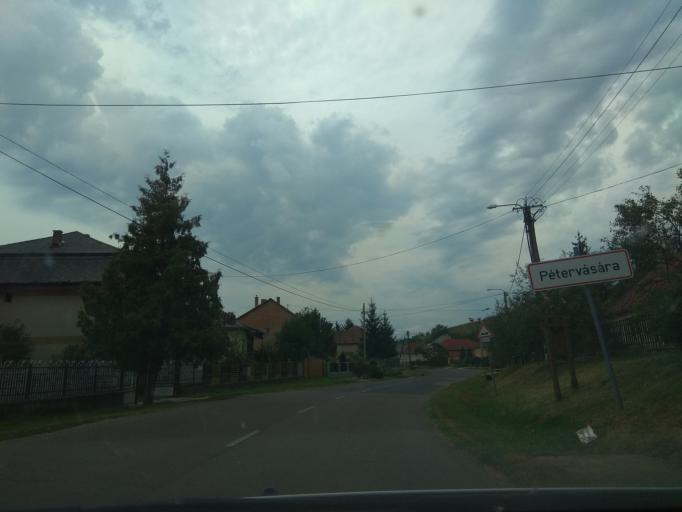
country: HU
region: Heves
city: Petervasara
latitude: 48.0316
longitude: 20.1042
